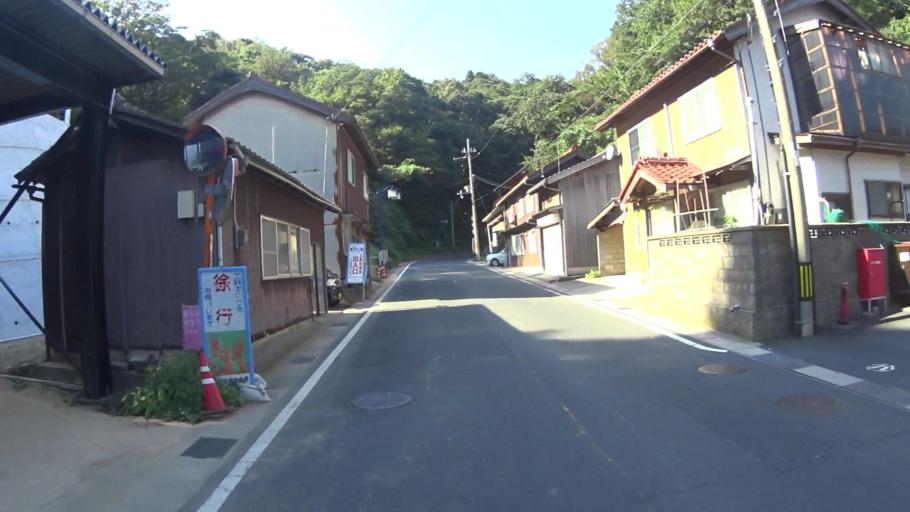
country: JP
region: Kyoto
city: Miyazu
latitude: 35.7323
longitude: 135.0943
